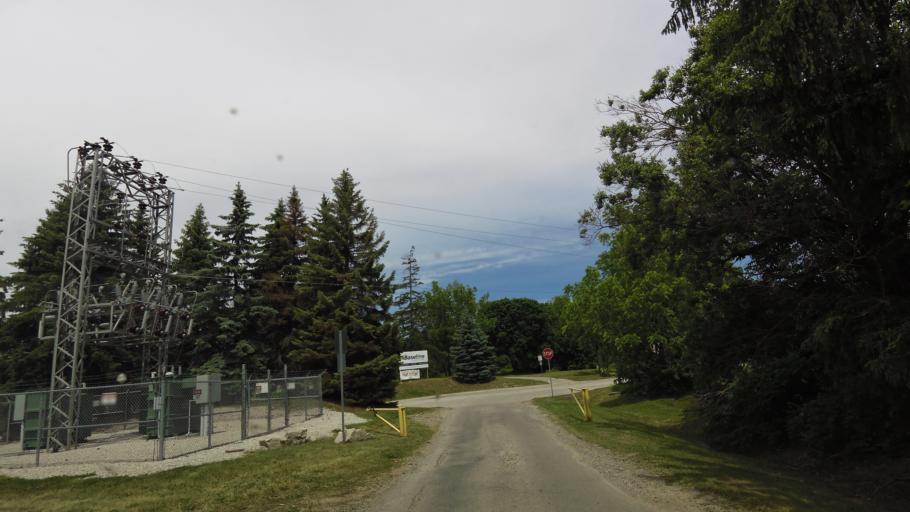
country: CA
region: Ontario
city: Oakville
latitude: 43.4815
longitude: -79.6309
